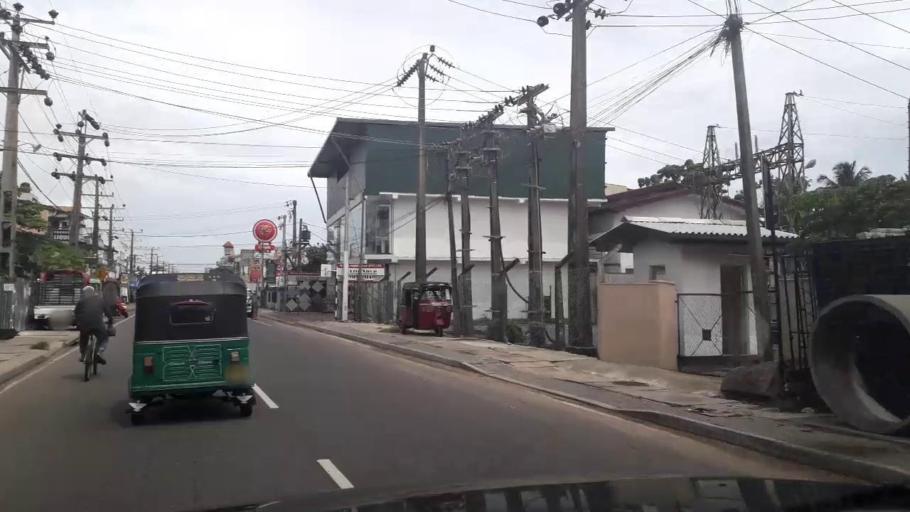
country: LK
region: Western
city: Panadura
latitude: 6.7428
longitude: 79.9025
